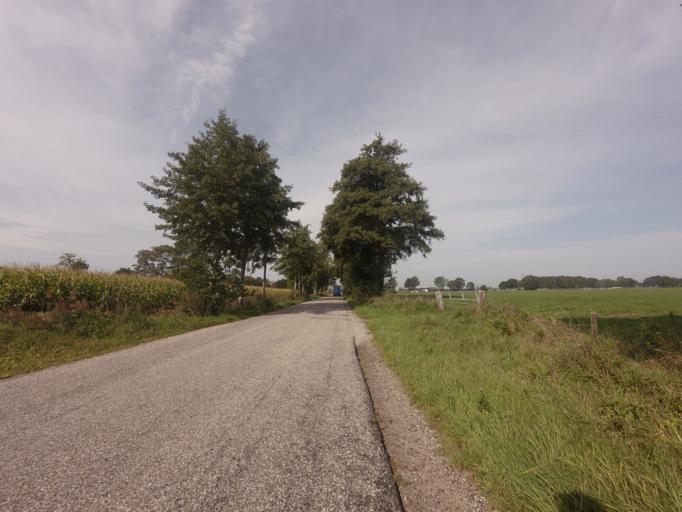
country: NL
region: Groningen
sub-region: Gemeente Leek
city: Leek
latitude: 53.1902
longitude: 6.3590
